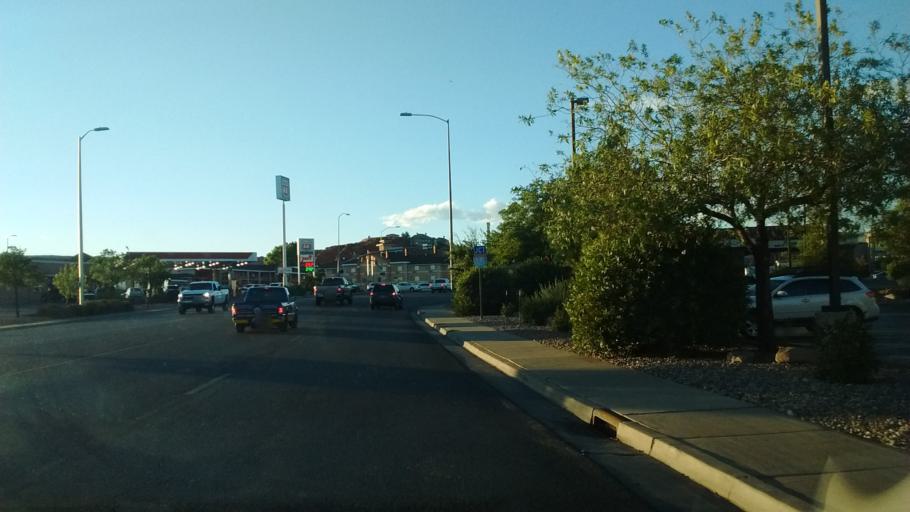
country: US
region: Utah
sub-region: Washington County
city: Washington
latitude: 37.1262
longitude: -113.5228
